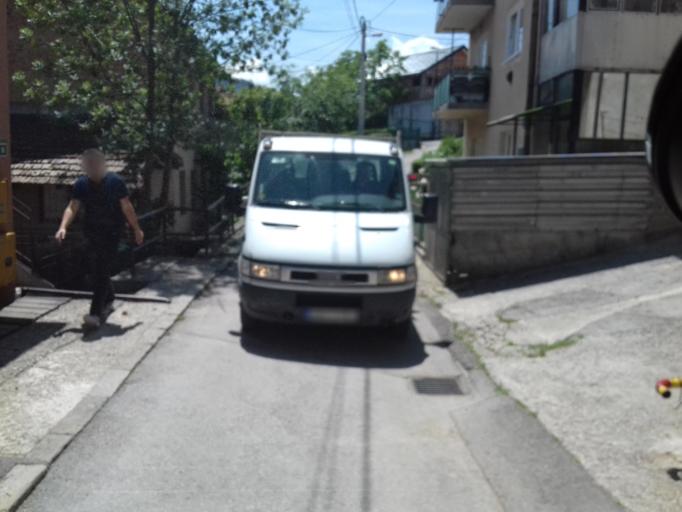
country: BA
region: Federation of Bosnia and Herzegovina
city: Kobilja Glava
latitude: 43.8669
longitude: 18.4254
